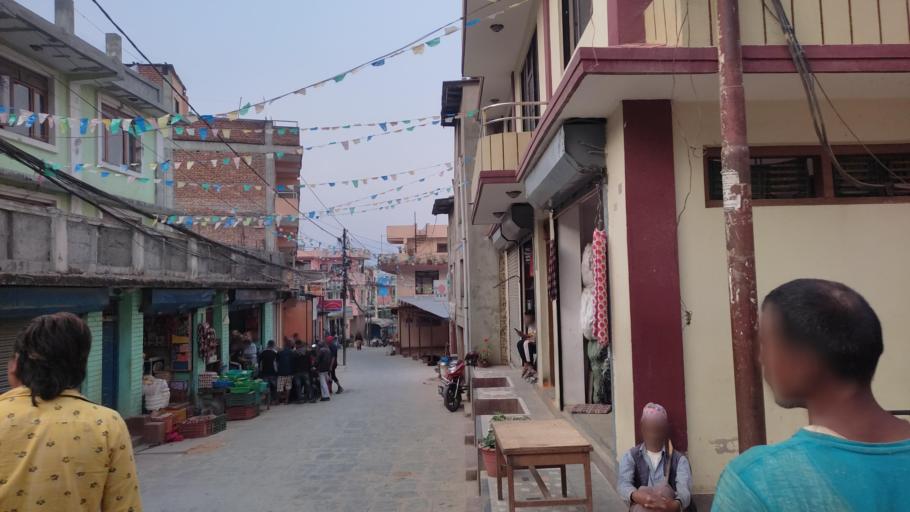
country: NP
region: Central Region
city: Kirtipur
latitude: 27.6685
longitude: 85.2494
